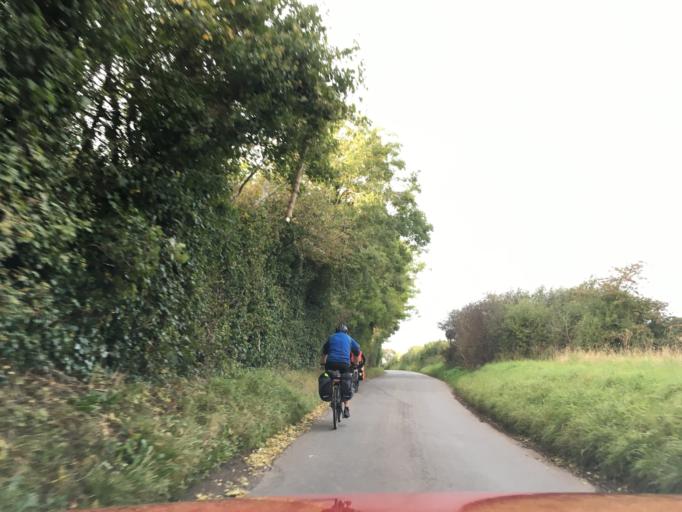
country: GB
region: England
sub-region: South Gloucestershire
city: Almondsbury
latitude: 51.5872
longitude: -2.5773
